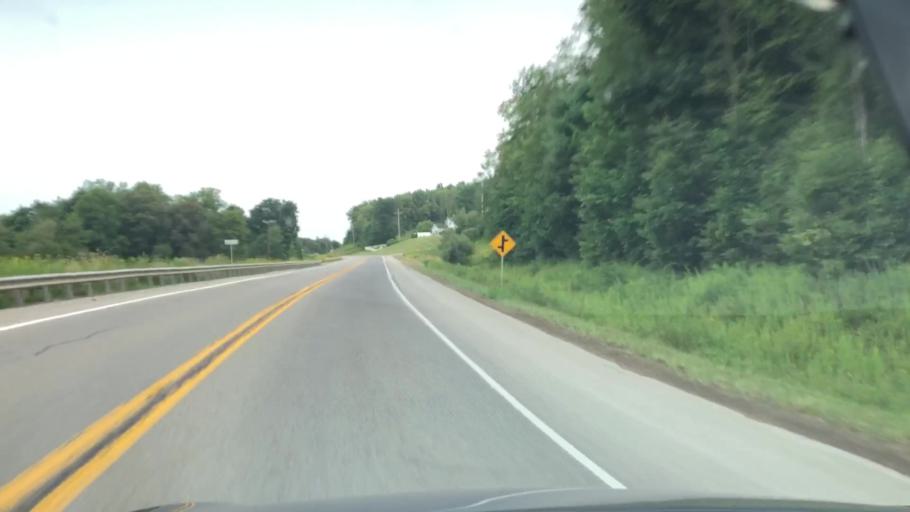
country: US
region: Pennsylvania
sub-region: Venango County
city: Hasson Heights
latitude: 41.5296
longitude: -79.7148
